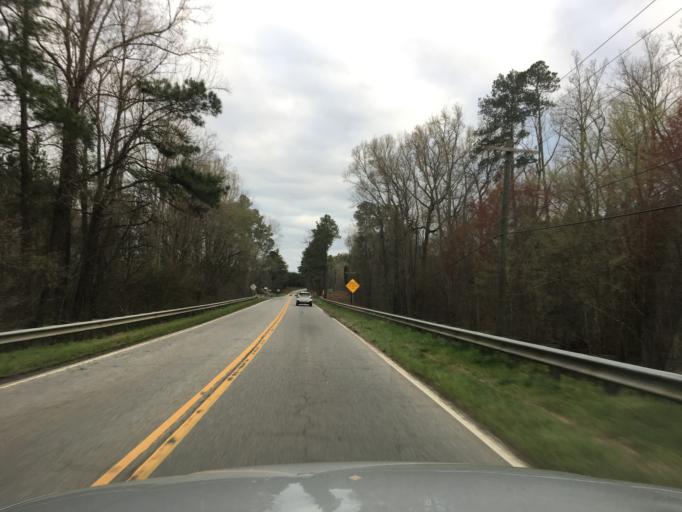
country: US
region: South Carolina
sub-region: Saluda County
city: Saluda
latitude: 33.9885
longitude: -81.7707
